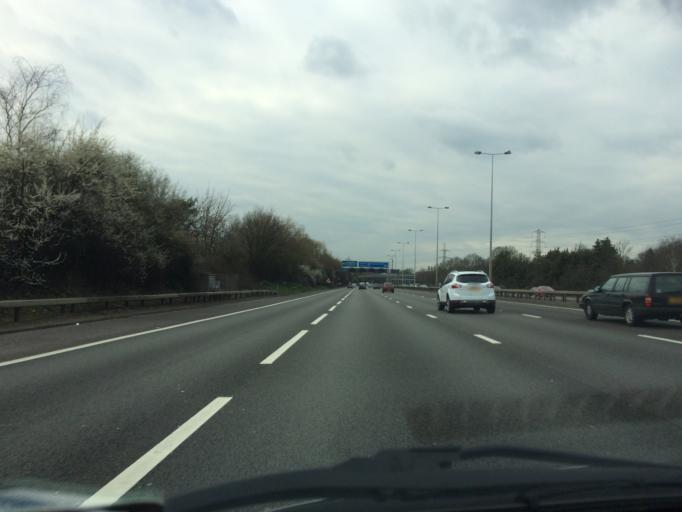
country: GB
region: England
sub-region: Surrey
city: Chertsey
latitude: 51.3869
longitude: -0.5235
